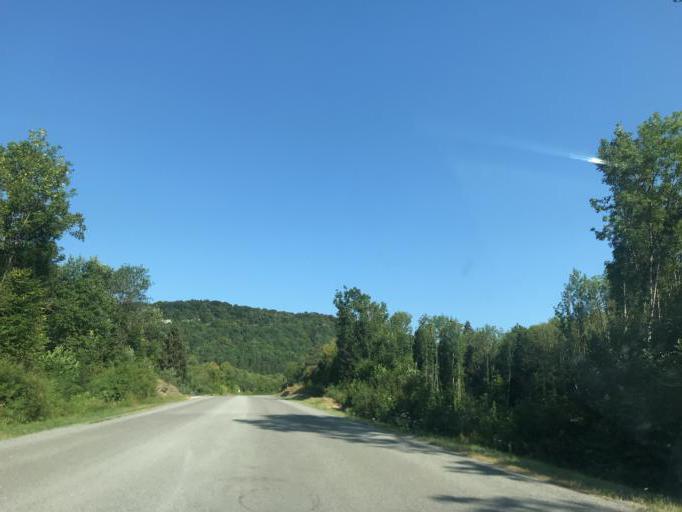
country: FR
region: Franche-Comte
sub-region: Departement du Jura
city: Lavans-les-Saint-Claude
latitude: 46.3831
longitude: 5.7496
